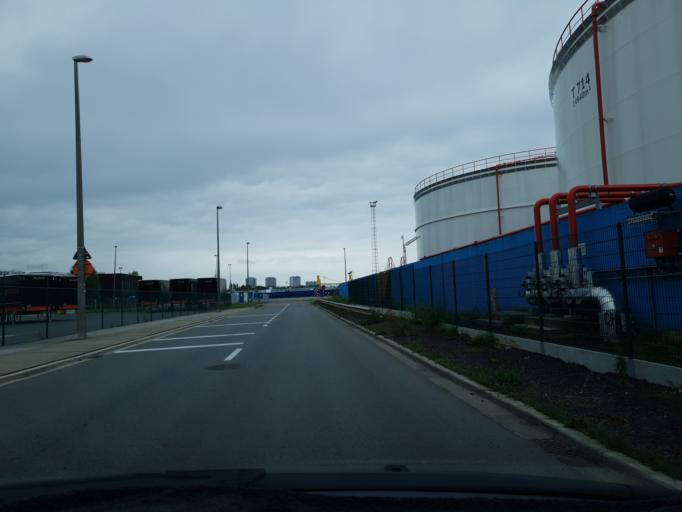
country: BE
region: Flanders
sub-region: Provincie Antwerpen
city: Antwerpen
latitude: 51.2507
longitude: 4.3840
